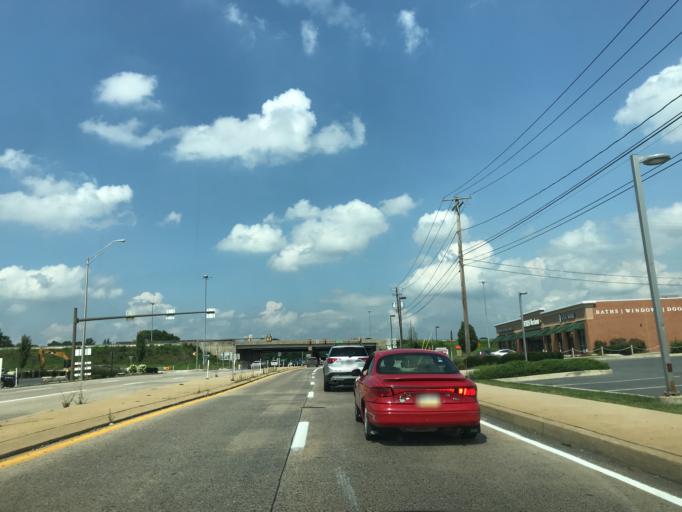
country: US
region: Pennsylvania
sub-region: Lancaster County
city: Lancaster
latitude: 40.0670
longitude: -76.3042
